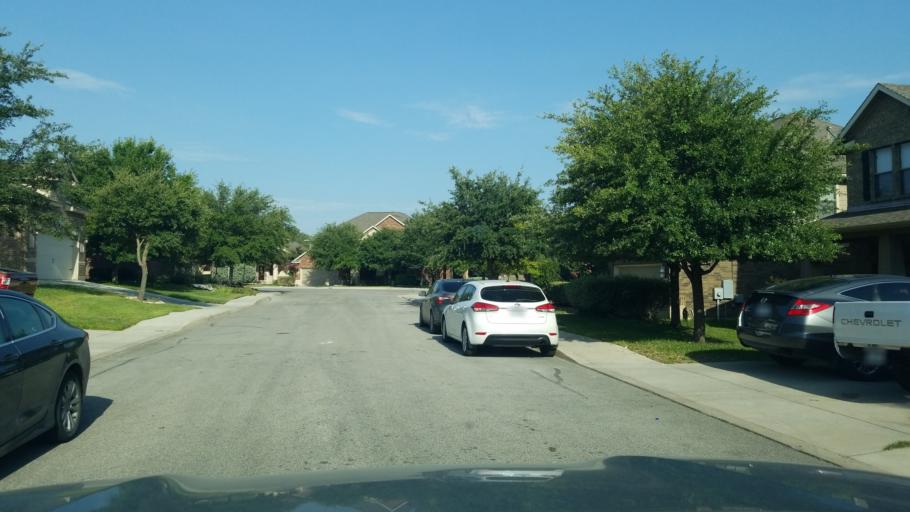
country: US
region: Texas
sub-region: Bexar County
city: Leon Valley
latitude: 29.4418
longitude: -98.7513
